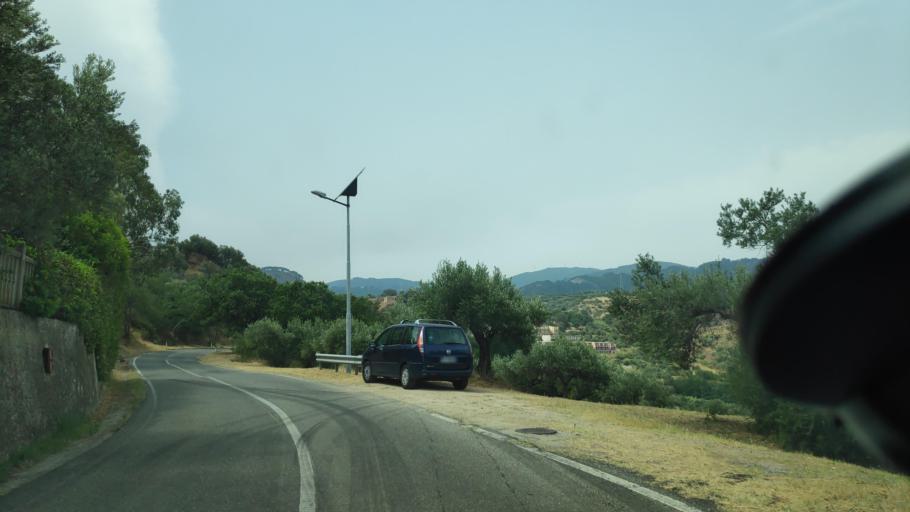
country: IT
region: Calabria
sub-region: Provincia di Catanzaro
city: Marina di Davoli
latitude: 38.6472
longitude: 16.5392
